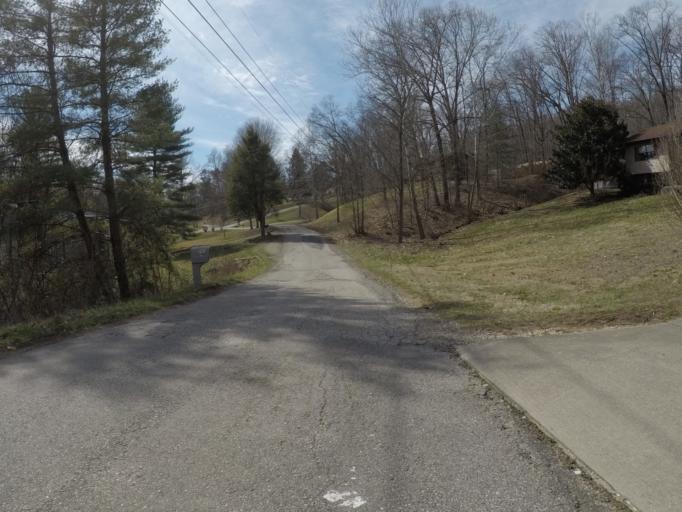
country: US
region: West Virginia
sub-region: Wayne County
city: Ceredo
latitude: 38.3632
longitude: -82.5327
